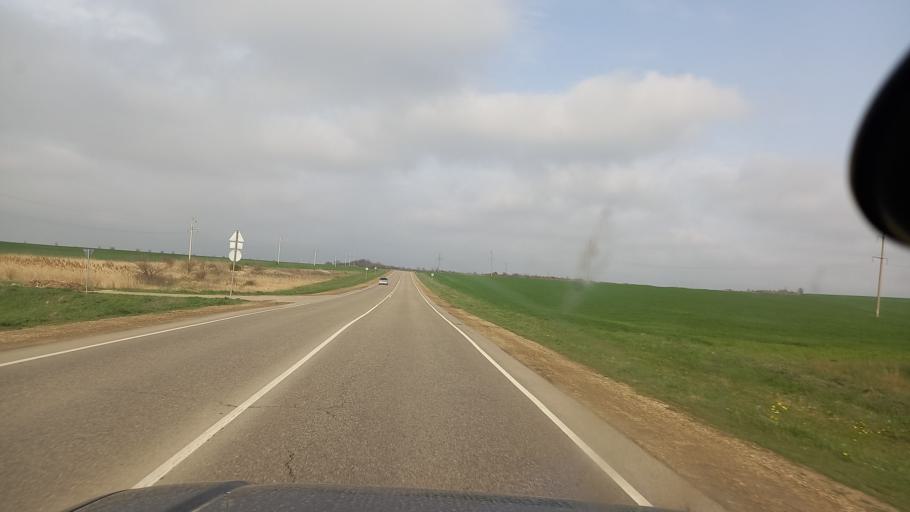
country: RU
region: Krasnodarskiy
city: Varenikovskaya
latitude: 45.0995
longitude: 37.5972
